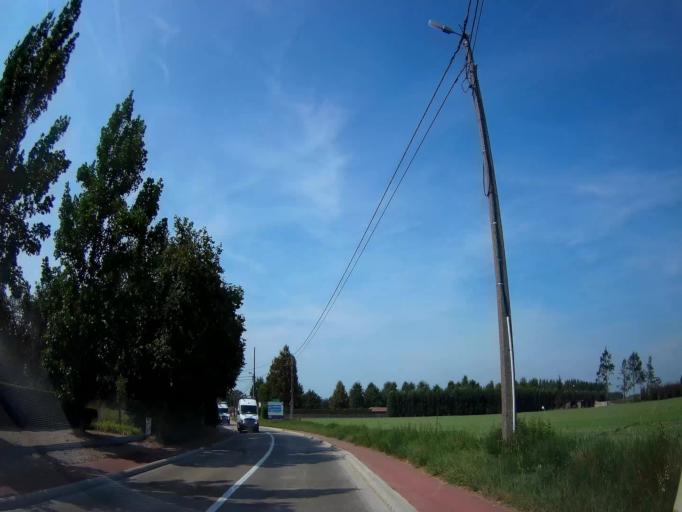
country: BE
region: Flanders
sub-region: Provincie Vlaams-Brabant
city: Zoutleeuw
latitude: 50.8264
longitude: 5.1275
